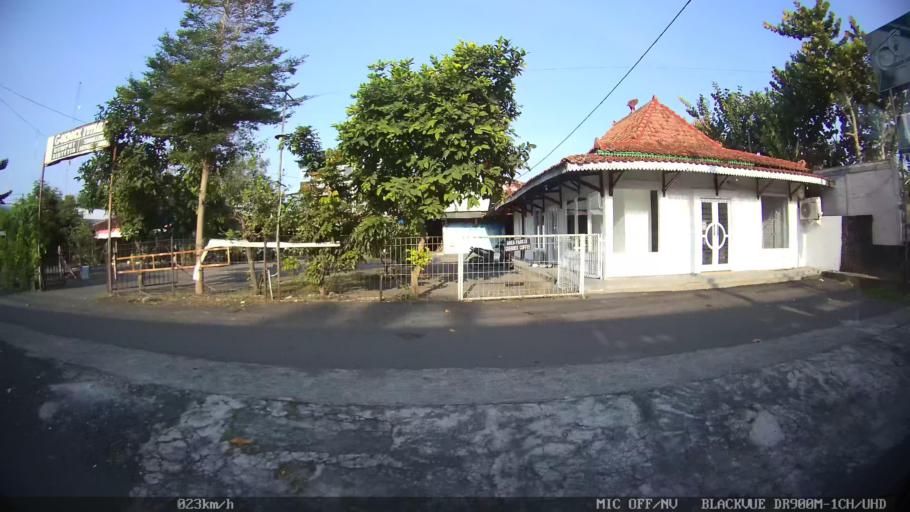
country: ID
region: Daerah Istimewa Yogyakarta
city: Depok
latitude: -7.7723
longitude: 110.4050
